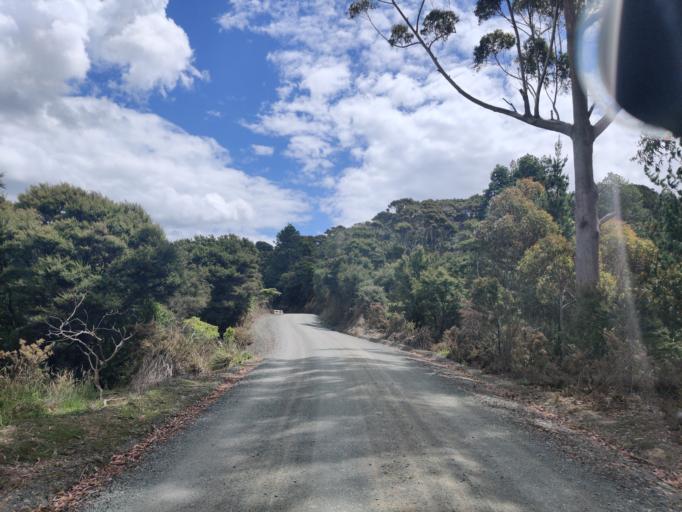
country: NZ
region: Northland
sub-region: Far North District
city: Paihia
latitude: -35.2603
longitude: 174.0507
